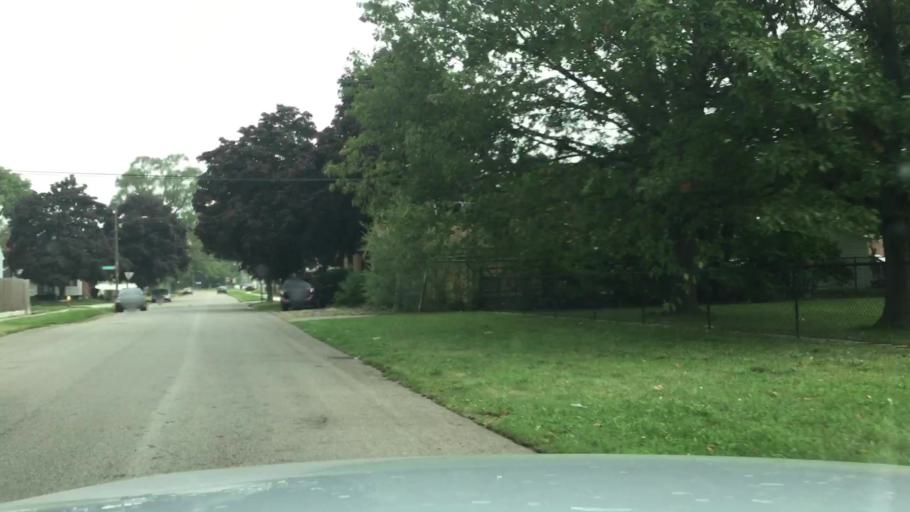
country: US
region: Michigan
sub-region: Macomb County
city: Eastpointe
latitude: 42.4472
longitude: -82.9734
